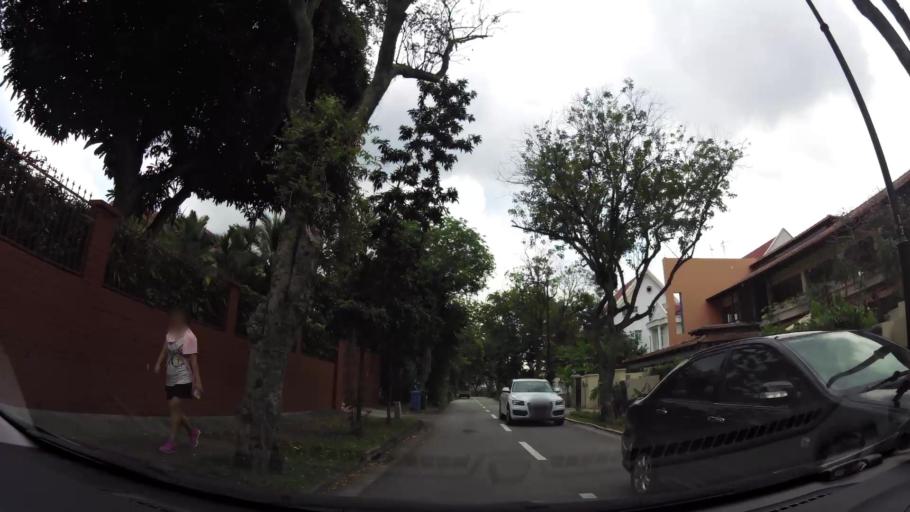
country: SG
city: Singapore
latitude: 1.3463
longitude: 103.8647
